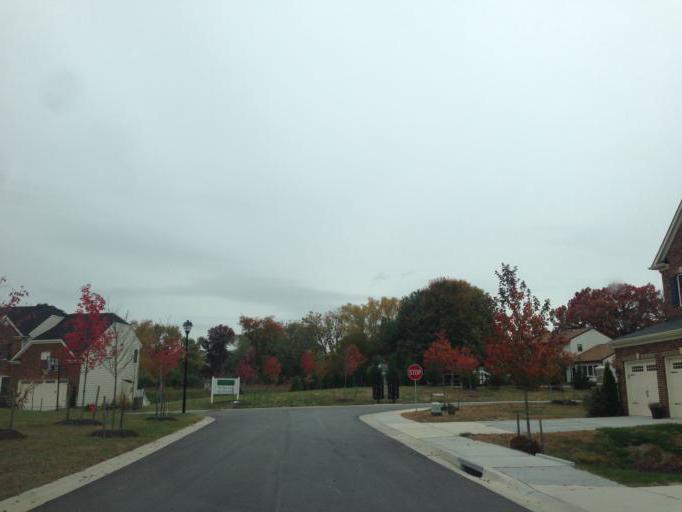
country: US
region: Maryland
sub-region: Howard County
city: Ellicott City
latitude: 39.2983
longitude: -76.8346
